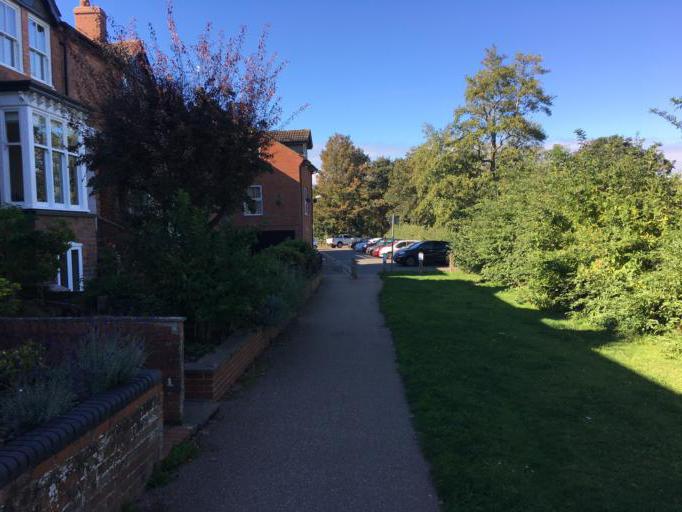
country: GB
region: England
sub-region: Warwickshire
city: Kenilworth
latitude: 52.3513
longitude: -1.5725
